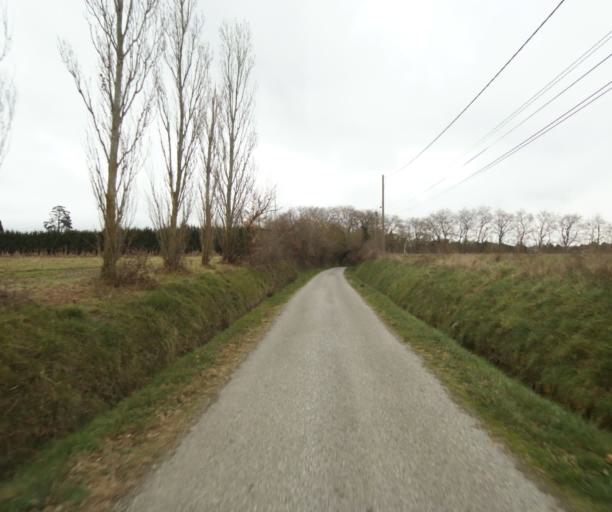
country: FR
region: Midi-Pyrenees
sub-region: Departement de l'Ariege
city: Mazeres
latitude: 43.2505
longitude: 1.6670
